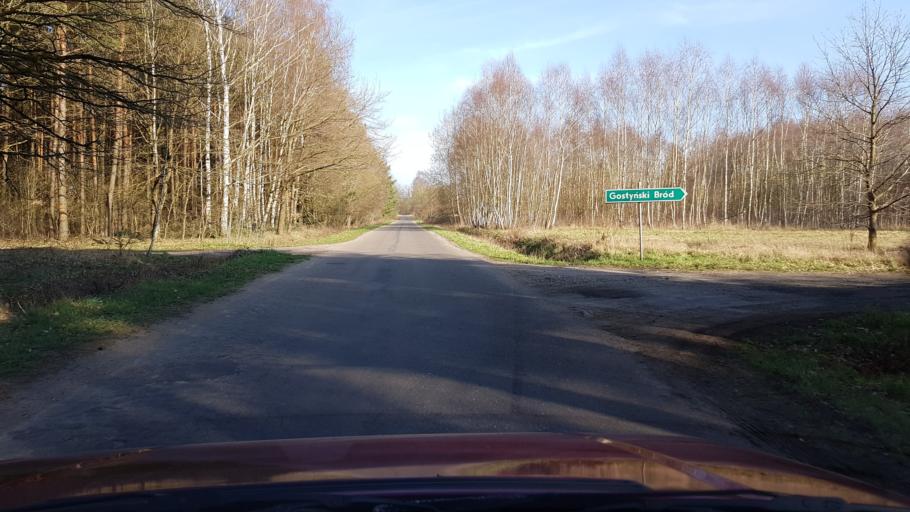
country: PL
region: West Pomeranian Voivodeship
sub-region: Powiat gryficki
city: Ploty
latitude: 53.8305
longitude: 15.3225
